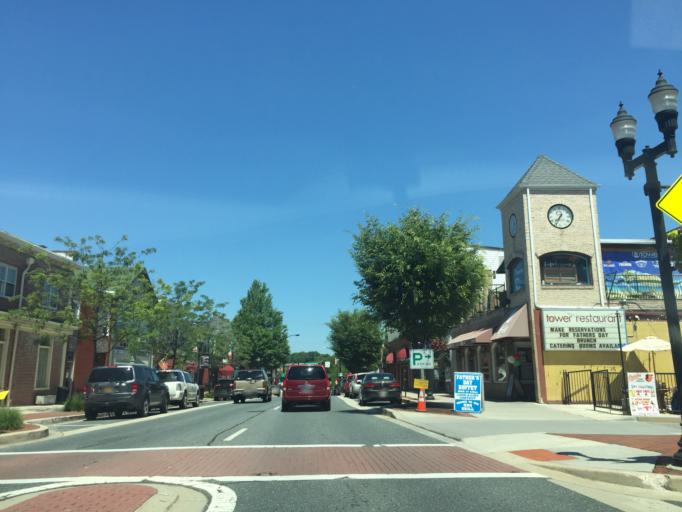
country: US
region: Maryland
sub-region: Harford County
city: Bel Air
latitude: 39.5359
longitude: -76.3487
